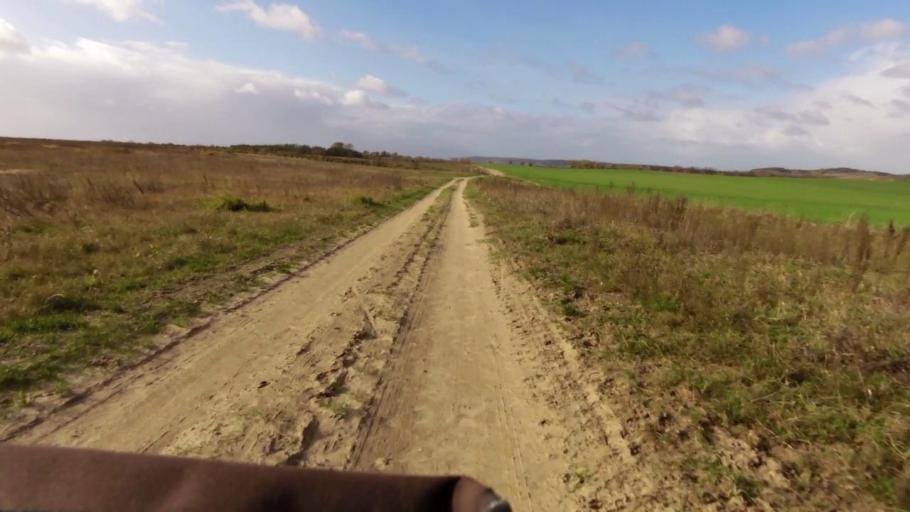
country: PL
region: West Pomeranian Voivodeship
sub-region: Powiat kamienski
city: Wolin
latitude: 53.8410
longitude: 14.5984
